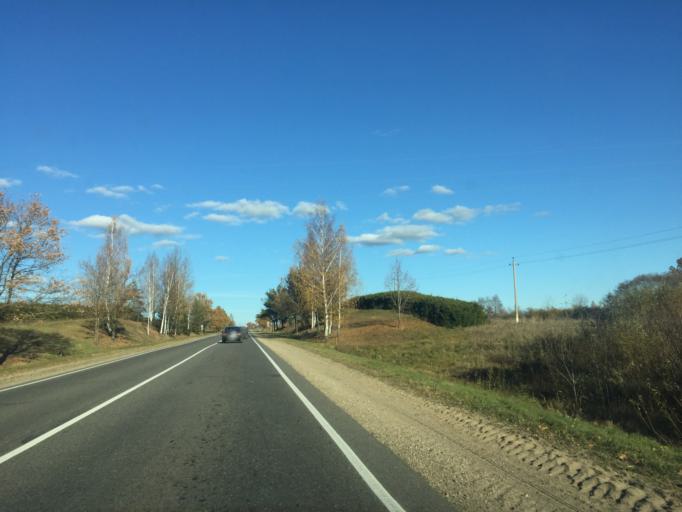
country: BY
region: Vitebsk
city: Dzisna
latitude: 55.2529
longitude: 28.1089
